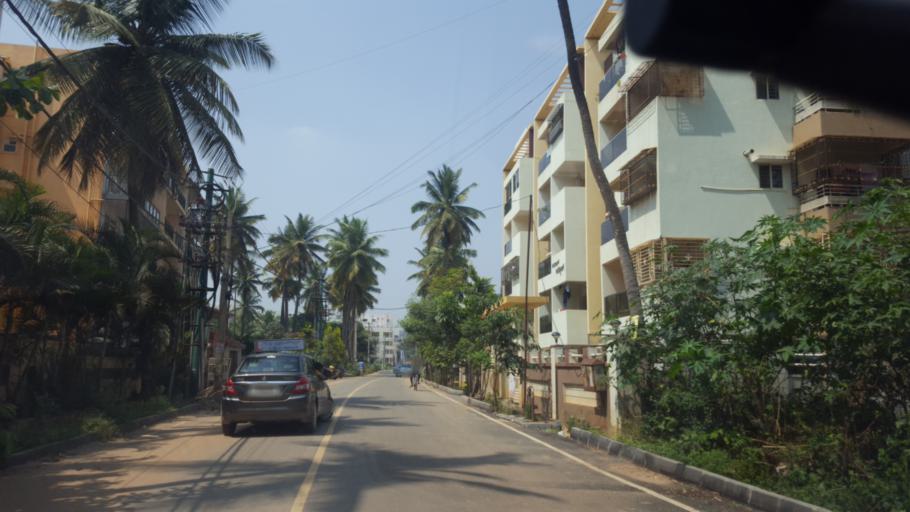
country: IN
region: Karnataka
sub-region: Bangalore Urban
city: Bangalore
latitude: 12.9404
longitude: 77.7050
